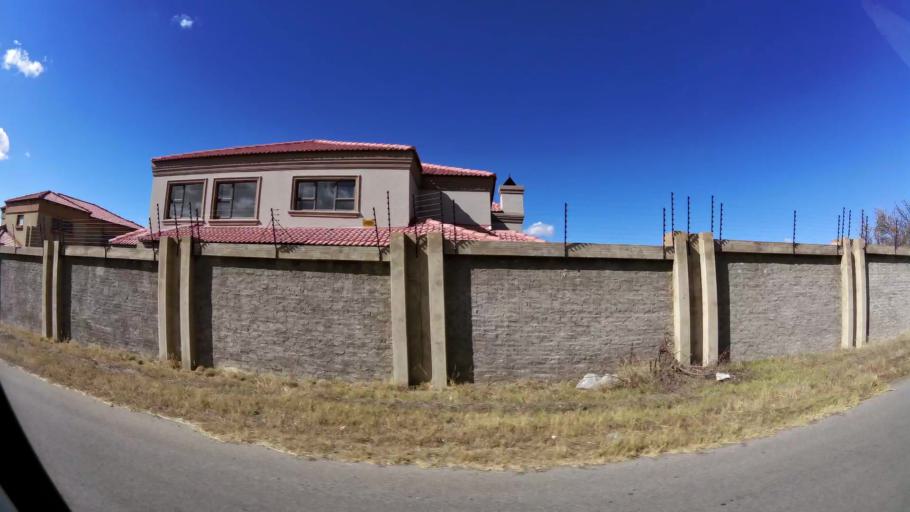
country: ZA
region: Limpopo
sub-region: Capricorn District Municipality
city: Polokwane
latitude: -23.8607
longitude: 29.5100
